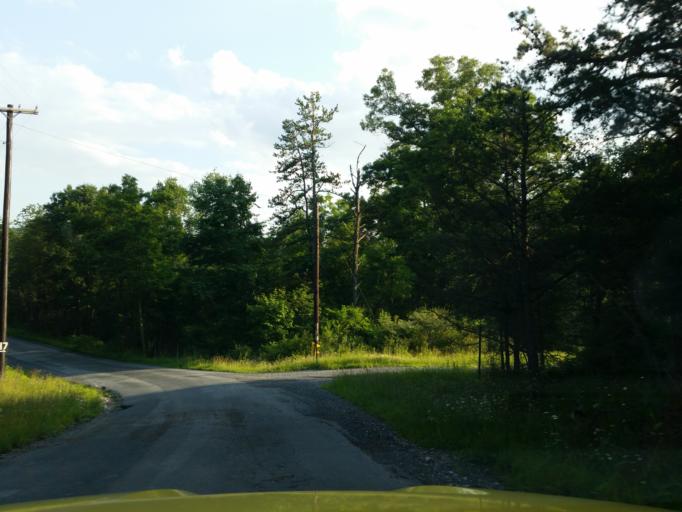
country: US
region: Pennsylvania
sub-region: Dauphin County
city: Williamstown
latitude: 40.4531
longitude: -76.6271
